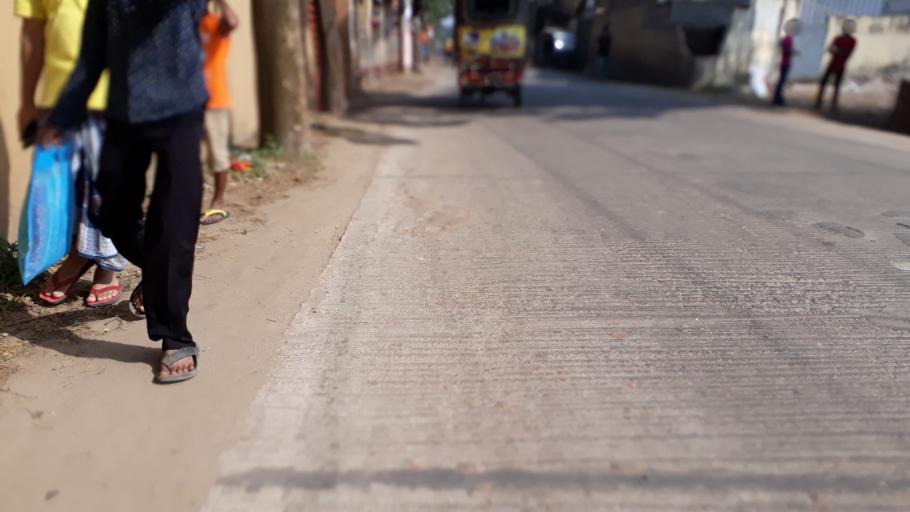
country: BD
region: Dhaka
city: Tungi
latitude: 23.8871
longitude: 90.3142
